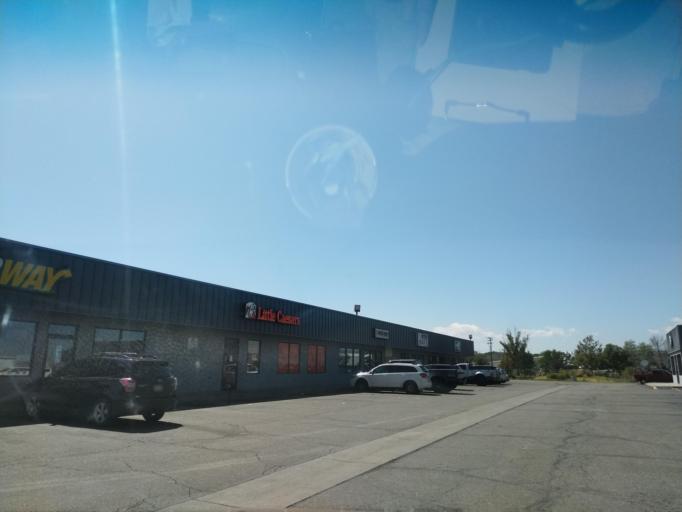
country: US
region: Colorado
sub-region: Delta County
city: Delta
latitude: 38.7468
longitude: -108.0712
